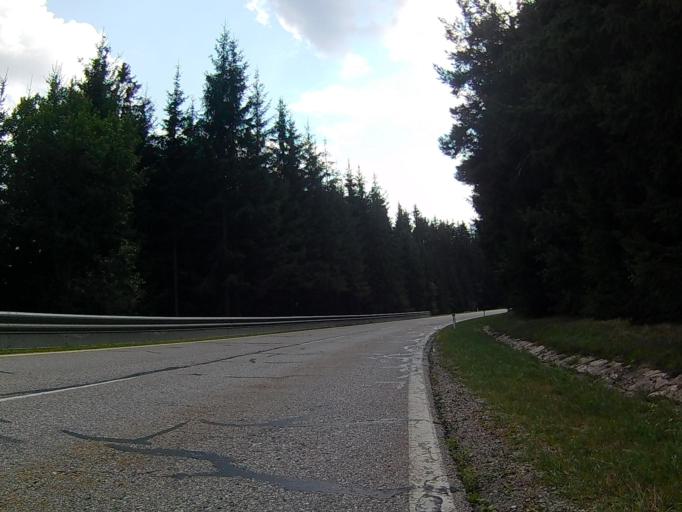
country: AT
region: Styria
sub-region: Politischer Bezirk Deutschlandsberg
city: Soboth
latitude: 46.6839
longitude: 15.0987
